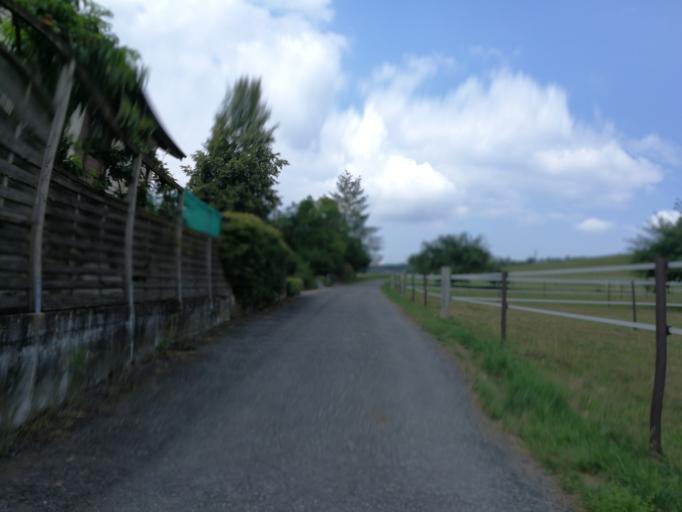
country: CH
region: Zurich
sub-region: Bezirk Hinwil
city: Gossau
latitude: 47.3242
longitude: 8.7588
